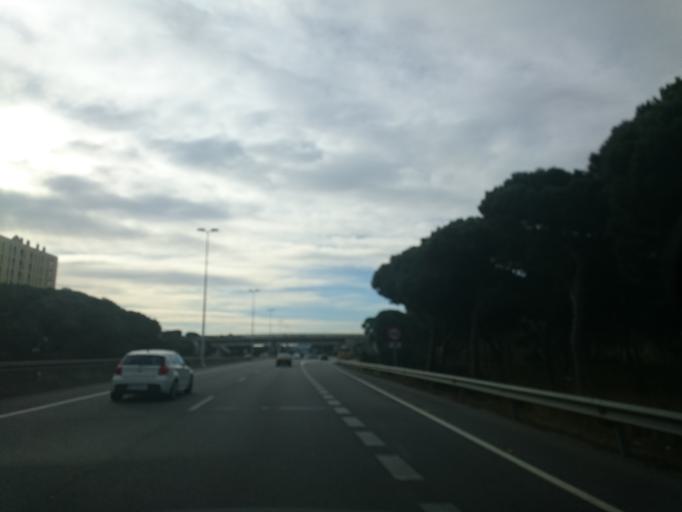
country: ES
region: Catalonia
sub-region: Provincia de Barcelona
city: Viladecans
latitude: 41.2722
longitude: 2.0398
